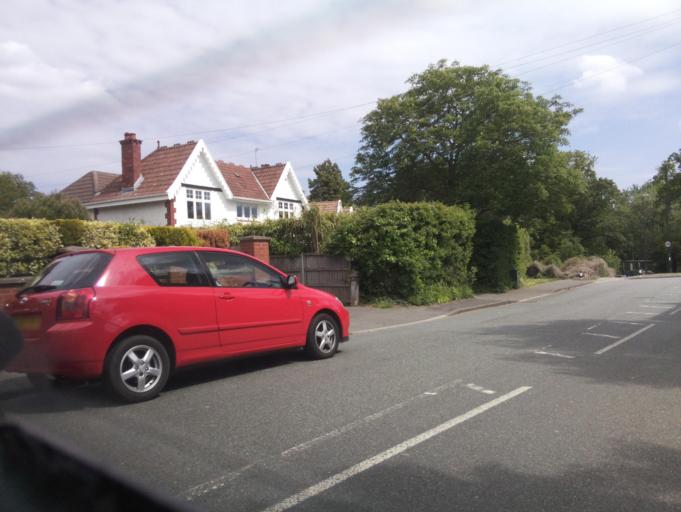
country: GB
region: England
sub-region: North Somerset
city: Easton-in-Gordano
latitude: 51.4926
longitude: -2.6436
